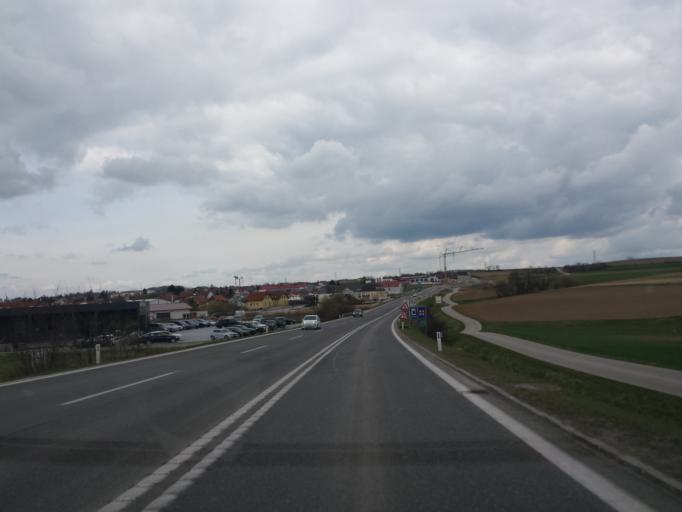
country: AT
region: Lower Austria
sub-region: Politischer Bezirk Krems
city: Gfohl
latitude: 48.5089
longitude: 15.5132
